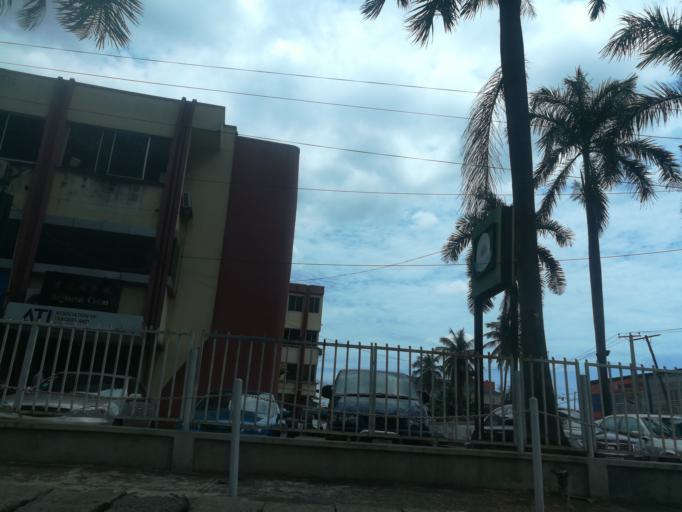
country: NG
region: Lagos
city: Ikeja
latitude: 6.5956
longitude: 3.3525
